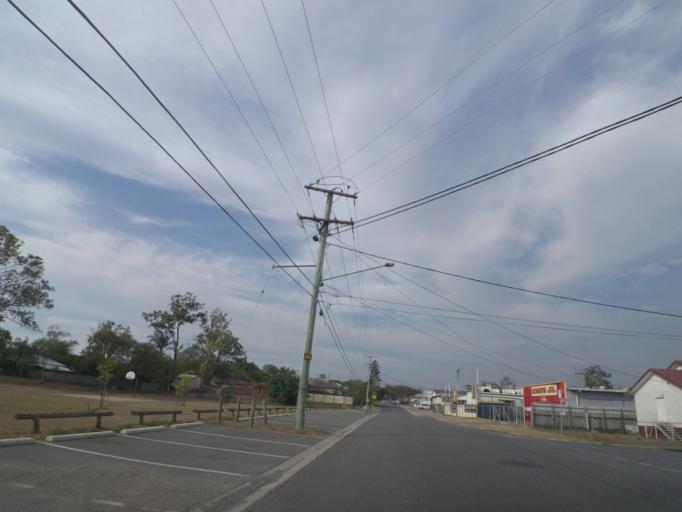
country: AU
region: Queensland
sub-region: Brisbane
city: Rocklea
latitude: -27.5460
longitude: 153.0185
